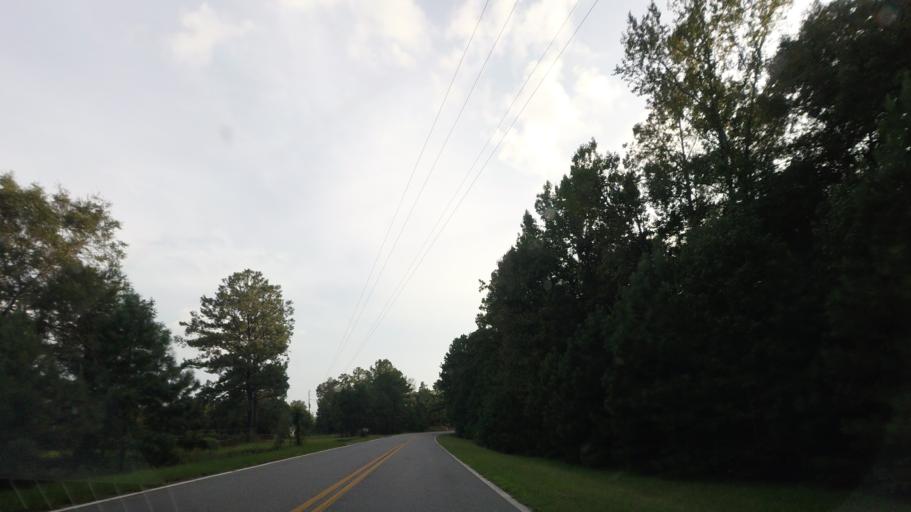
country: US
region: Georgia
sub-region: Wilkinson County
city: Gordon
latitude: 32.8225
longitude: -83.3946
